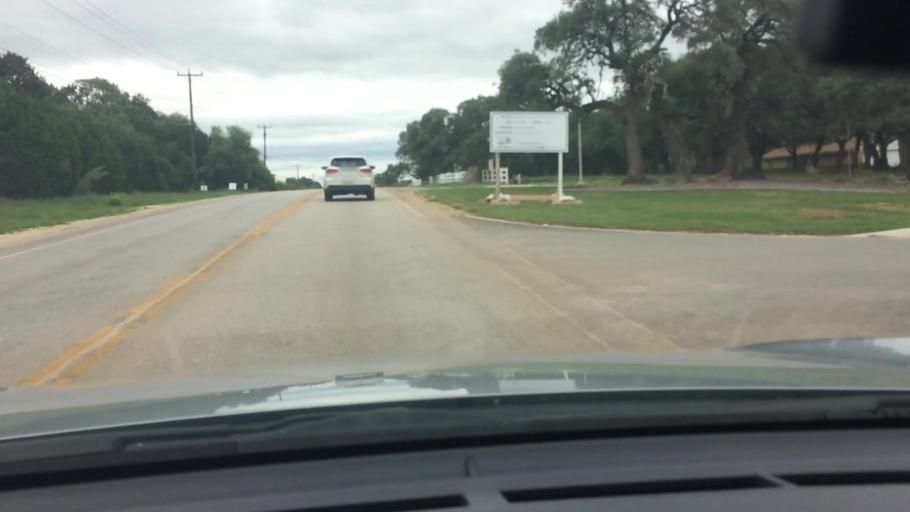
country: US
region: Texas
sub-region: Comal County
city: Garden Ridge
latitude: 29.6362
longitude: -98.3760
